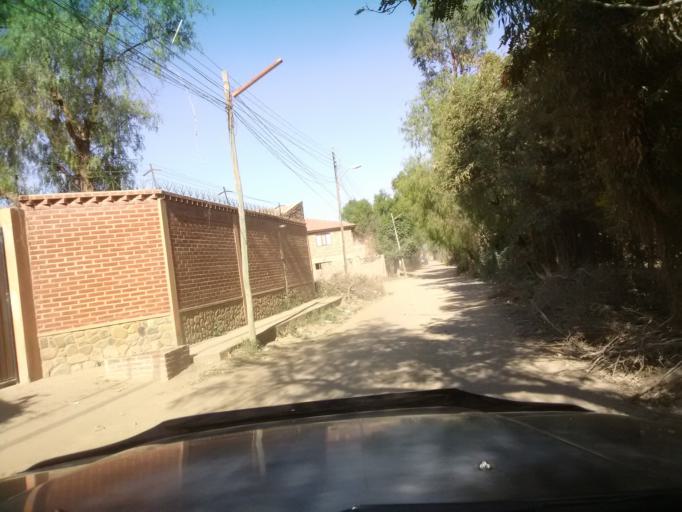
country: BO
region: Cochabamba
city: Cochabamba
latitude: -17.3569
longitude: -66.2054
